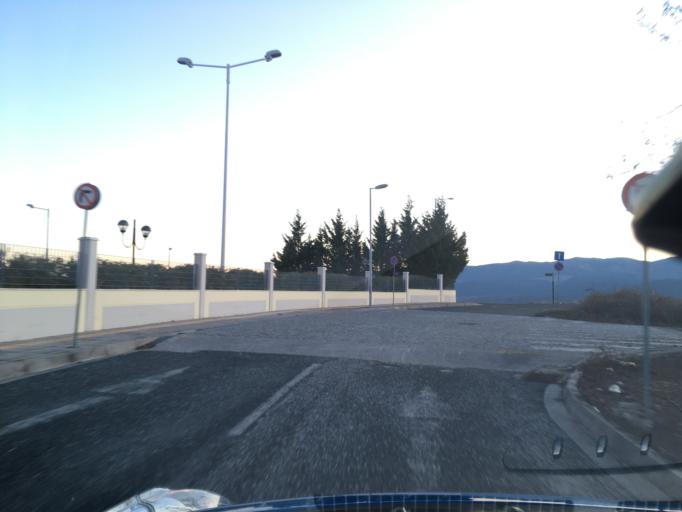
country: GR
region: West Macedonia
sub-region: Nomos Kozanis
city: Kozani
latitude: 40.2714
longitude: 21.7565
